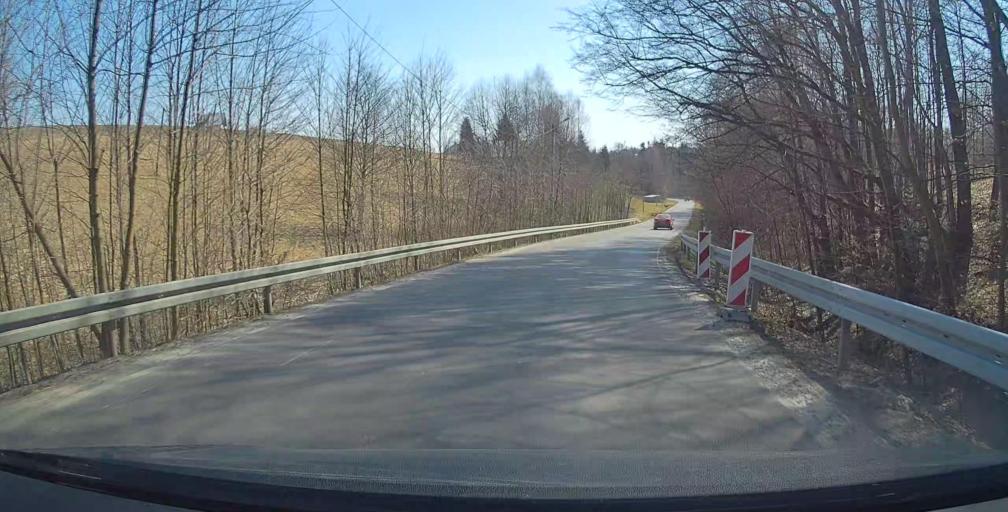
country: PL
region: Subcarpathian Voivodeship
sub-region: Powiat rzeszowski
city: Hyzne
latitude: 49.8943
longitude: 22.2232
